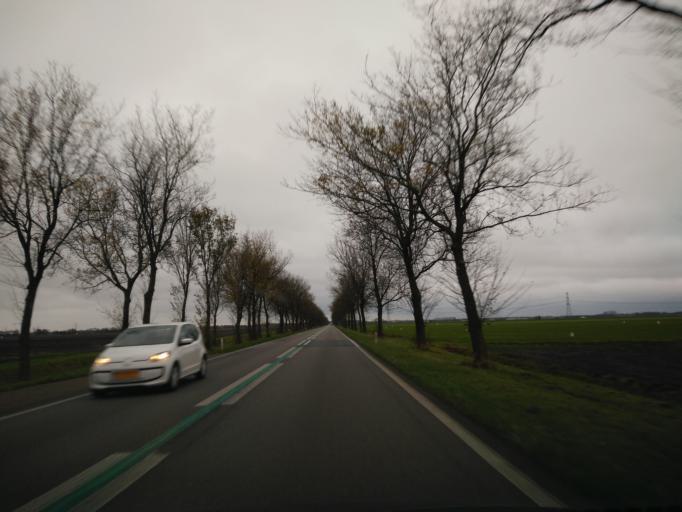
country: NL
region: Groningen
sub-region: Gemeente Stadskanaal
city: Stadskanaal
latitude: 53.0391
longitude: 6.9784
